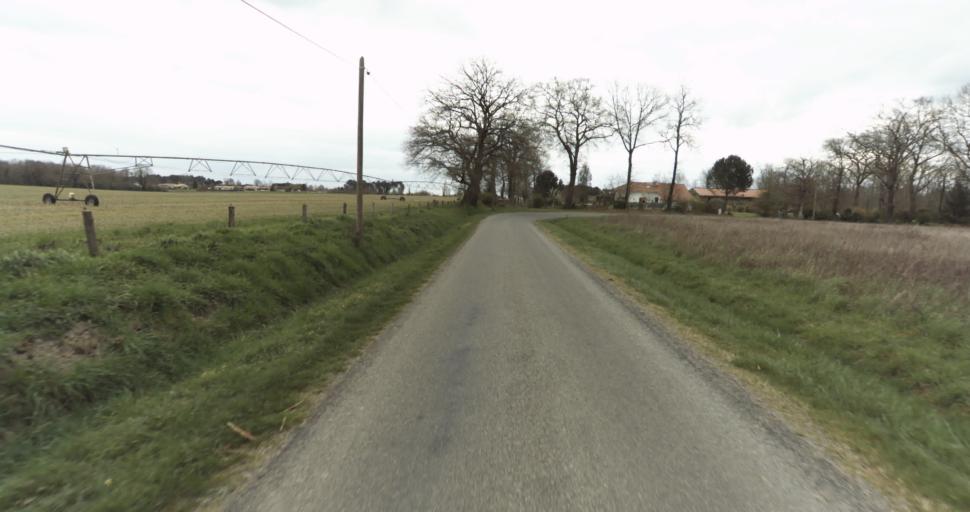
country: FR
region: Aquitaine
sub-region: Departement des Landes
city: Roquefort
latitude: 44.0163
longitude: -0.3349
